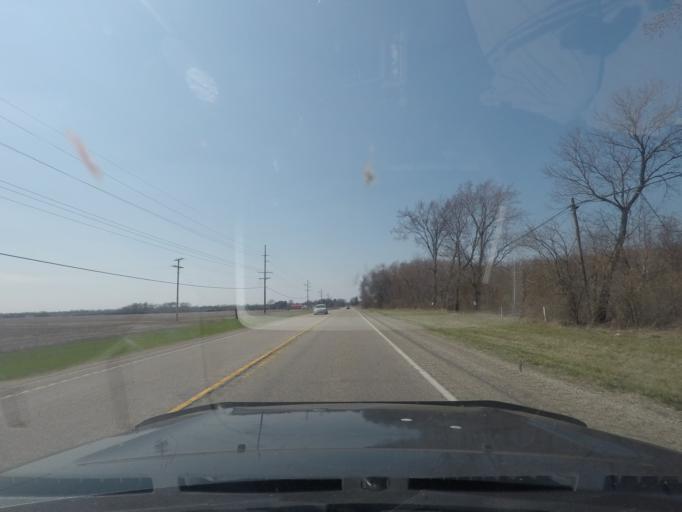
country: US
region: Indiana
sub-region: LaPorte County
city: LaPorte
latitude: 41.5915
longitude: -86.7889
